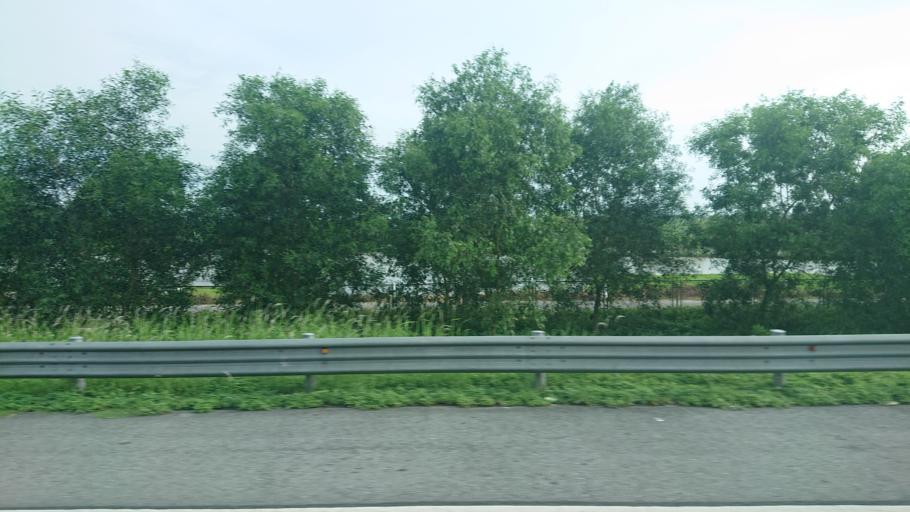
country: VN
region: Hai Phong
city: An Lao
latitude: 20.7991
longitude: 106.5368
